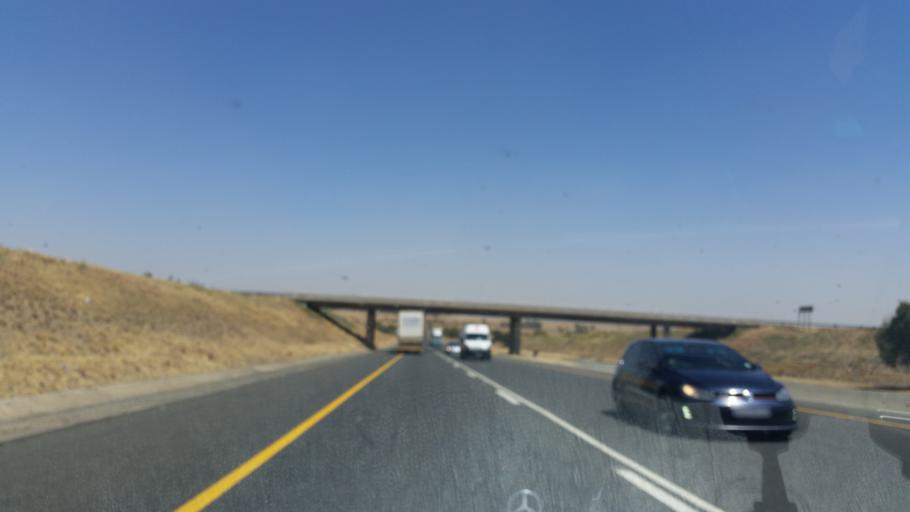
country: ZA
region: Orange Free State
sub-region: Lejweleputswa District Municipality
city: Winburg
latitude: -28.6266
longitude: 26.9110
